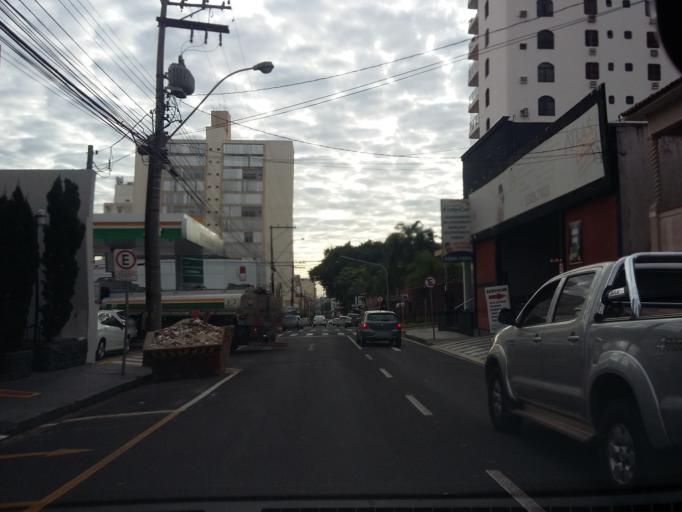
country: BR
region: Sao Paulo
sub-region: Sao Jose Do Rio Preto
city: Sao Jose do Rio Preto
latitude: -20.8169
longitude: -49.3865
